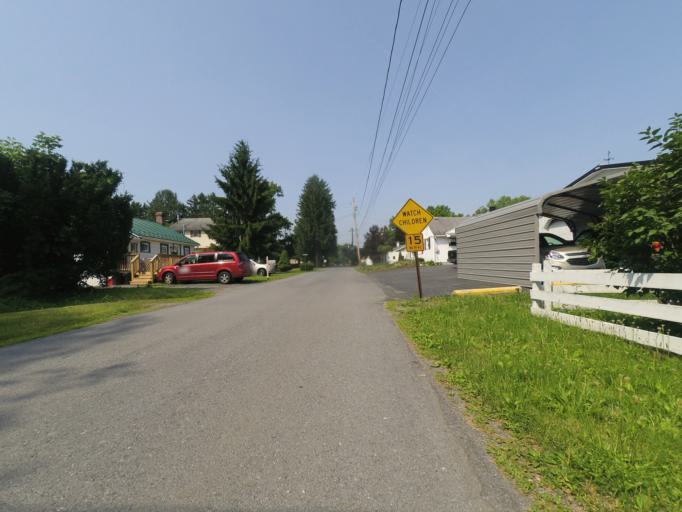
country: US
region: Pennsylvania
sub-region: Centre County
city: Milesburg
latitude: 40.9457
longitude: -77.7752
